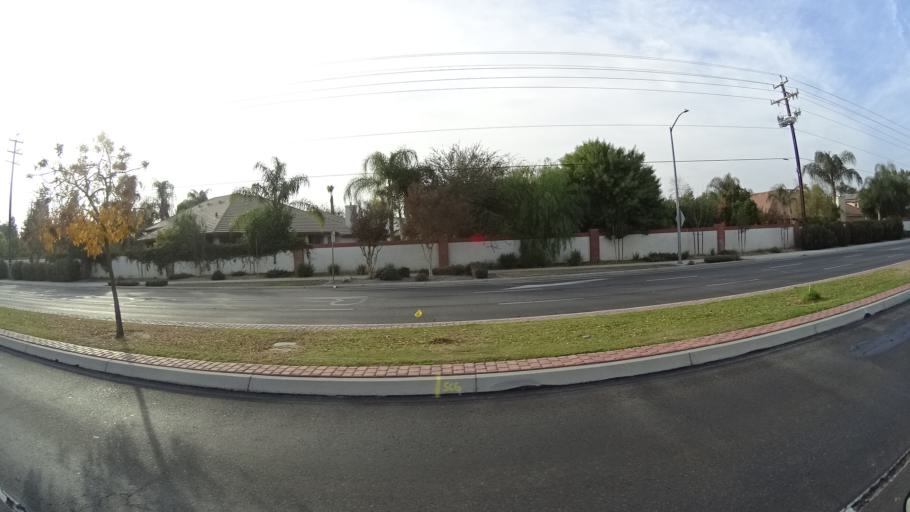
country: US
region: California
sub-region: Kern County
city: Greenacres
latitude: 35.3363
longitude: -119.1278
